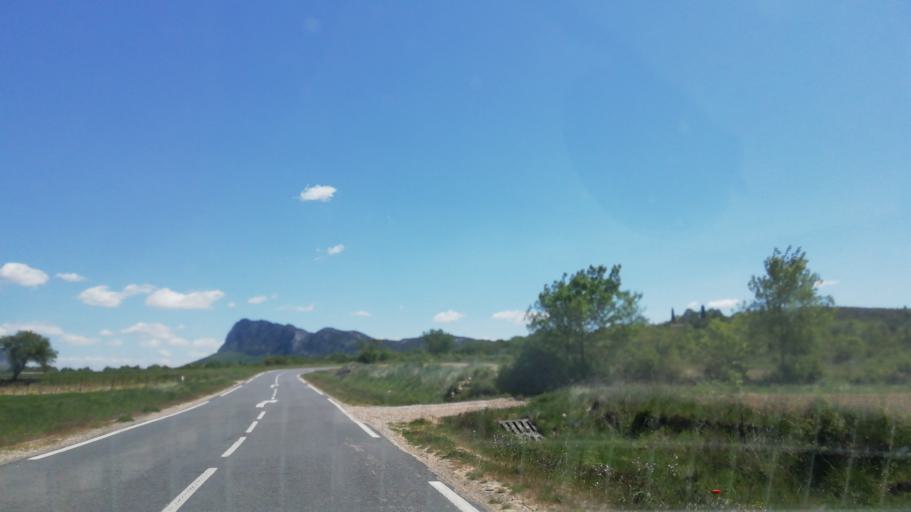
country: FR
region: Languedoc-Roussillon
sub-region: Departement de l'Herault
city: Saint-Martin-de-Londres
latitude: 43.7851
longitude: 3.7469
